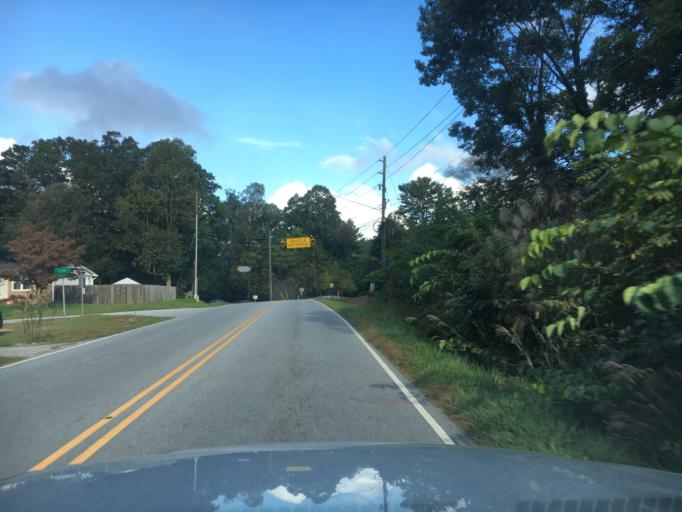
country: US
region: North Carolina
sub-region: Henderson County
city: Fletcher
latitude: 35.4353
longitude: -82.5159
